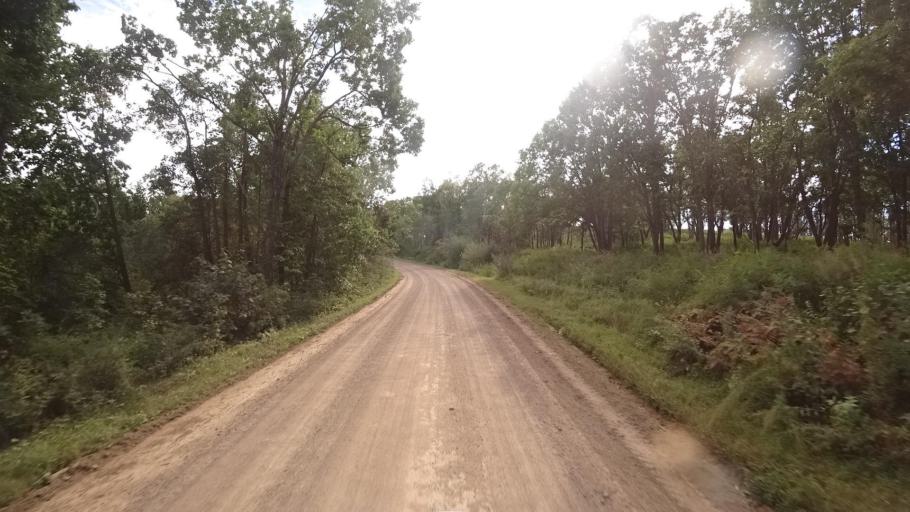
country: RU
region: Primorskiy
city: Dostoyevka
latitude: 44.3546
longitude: 133.5216
